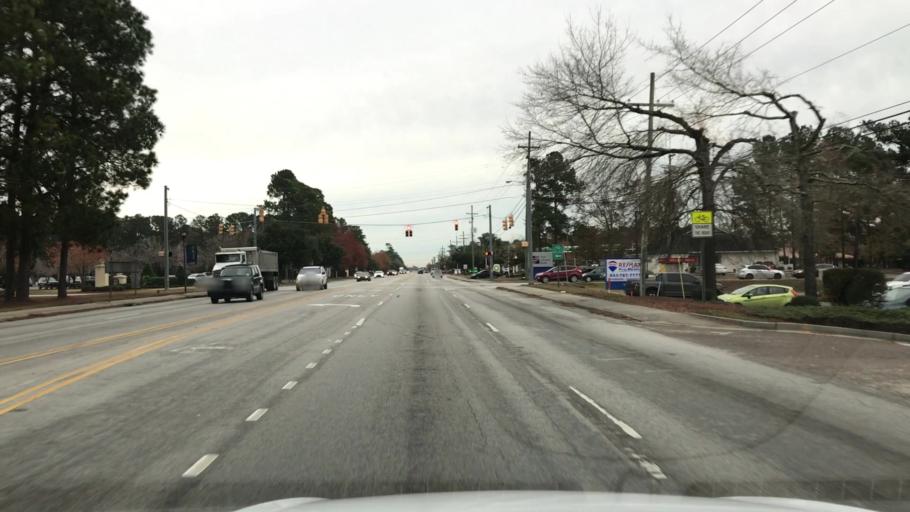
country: US
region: South Carolina
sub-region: Berkeley County
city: Goose Creek
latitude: 32.9775
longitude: -80.0714
